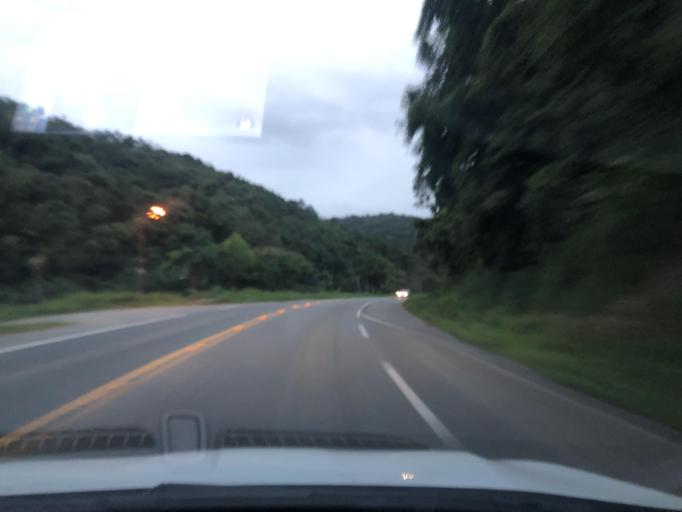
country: BR
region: Santa Catarina
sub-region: Pomerode
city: Pomerode
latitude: -26.6836
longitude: -49.0419
